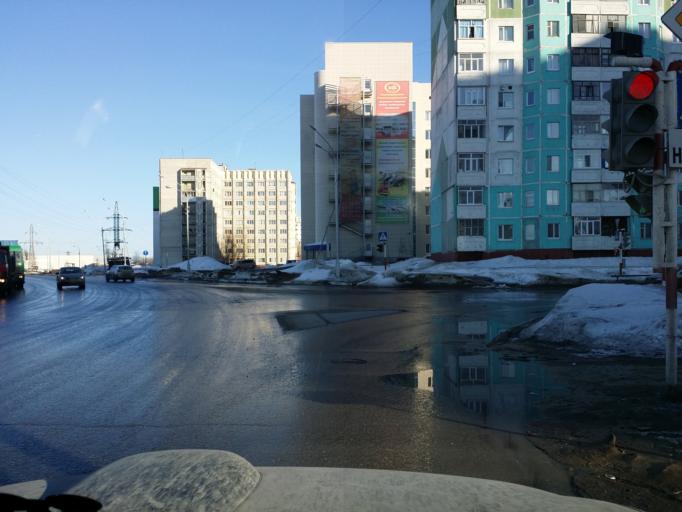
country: RU
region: Khanty-Mansiyskiy Avtonomnyy Okrug
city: Nizhnevartovsk
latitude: 60.9542
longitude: 76.5914
